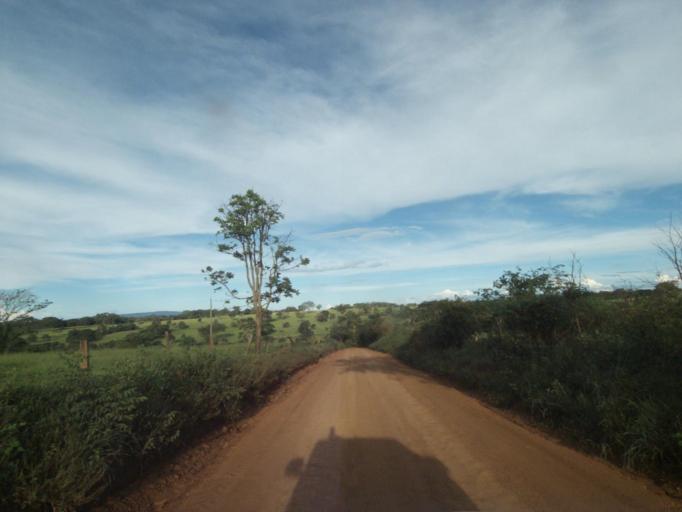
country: BR
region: Goias
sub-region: Jaragua
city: Jaragua
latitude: -15.8889
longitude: -49.4685
